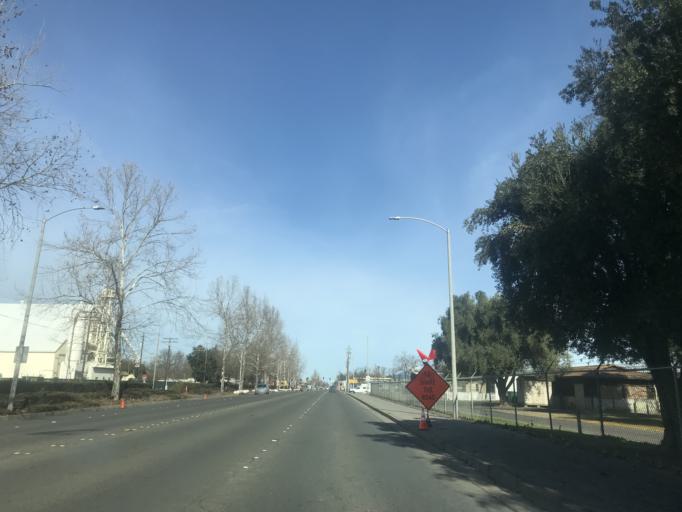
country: US
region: California
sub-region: Yolo County
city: Woodland
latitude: 38.6651
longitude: -121.7656
